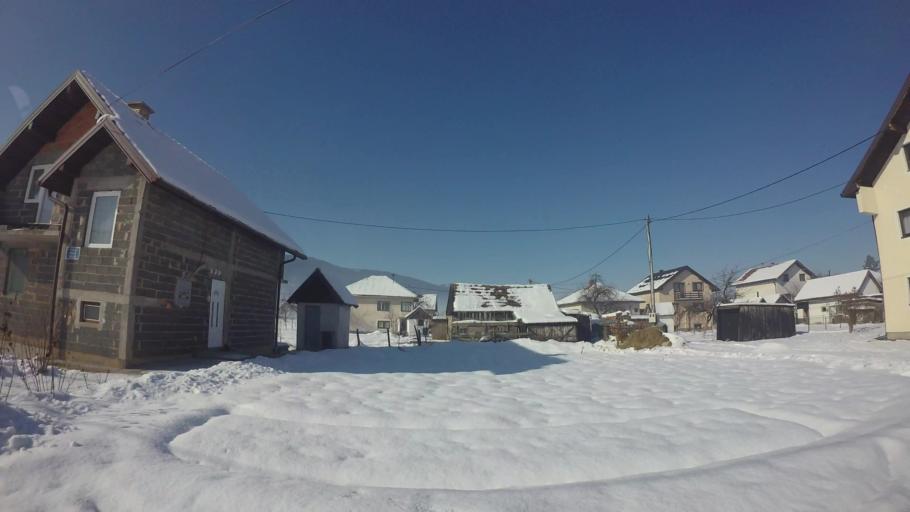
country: BA
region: Federation of Bosnia and Herzegovina
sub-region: Kanton Sarajevo
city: Sarajevo
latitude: 43.7940
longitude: 18.3403
